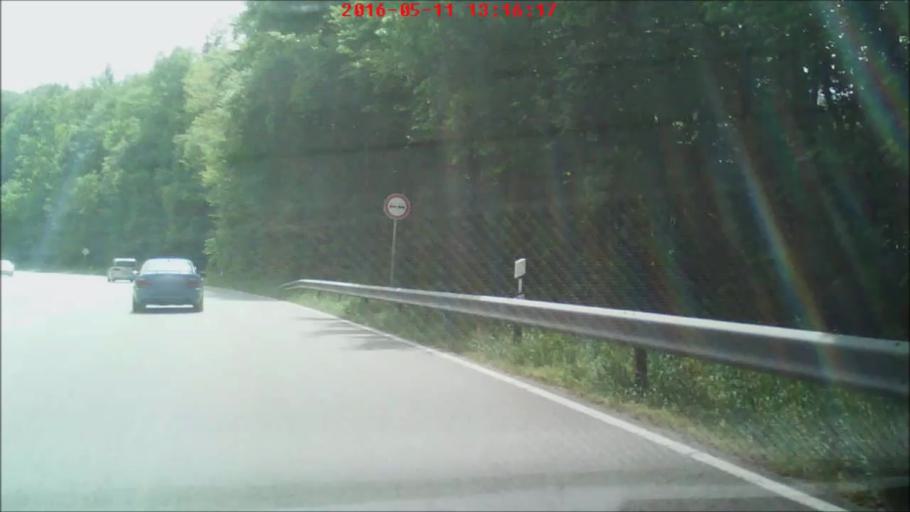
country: DE
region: Bavaria
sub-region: Lower Bavaria
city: Passau
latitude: 48.5511
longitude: 13.4074
